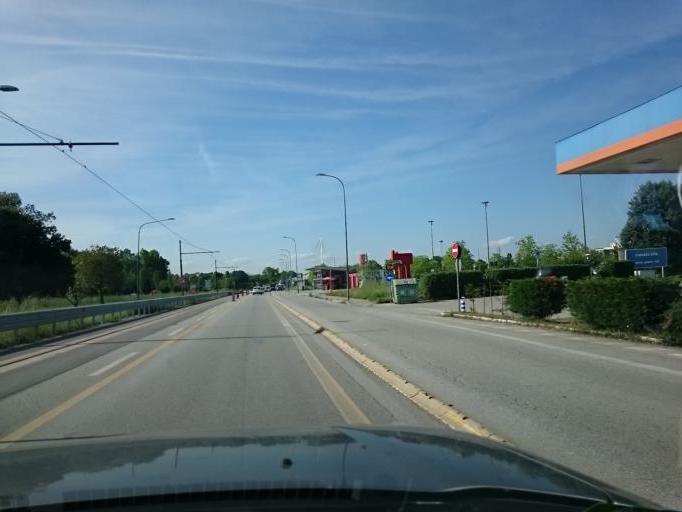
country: IT
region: Veneto
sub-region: Provincia di Venezia
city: Campalto
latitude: 45.4745
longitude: 12.2686
